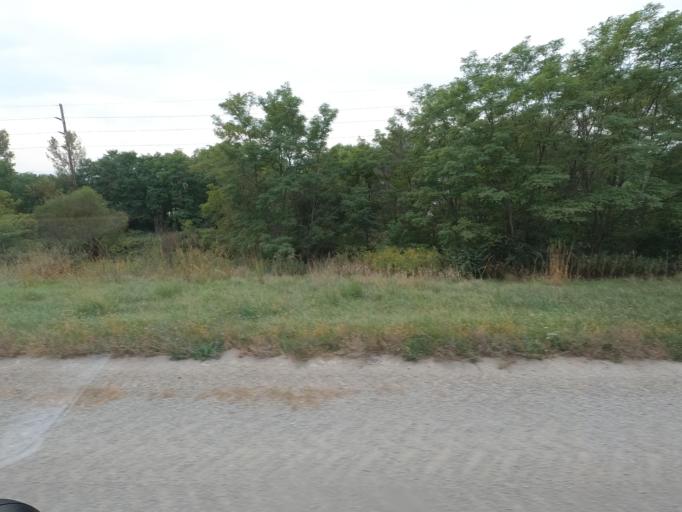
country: US
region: Iowa
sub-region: Marion County
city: Pella
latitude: 41.3961
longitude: -92.9319
